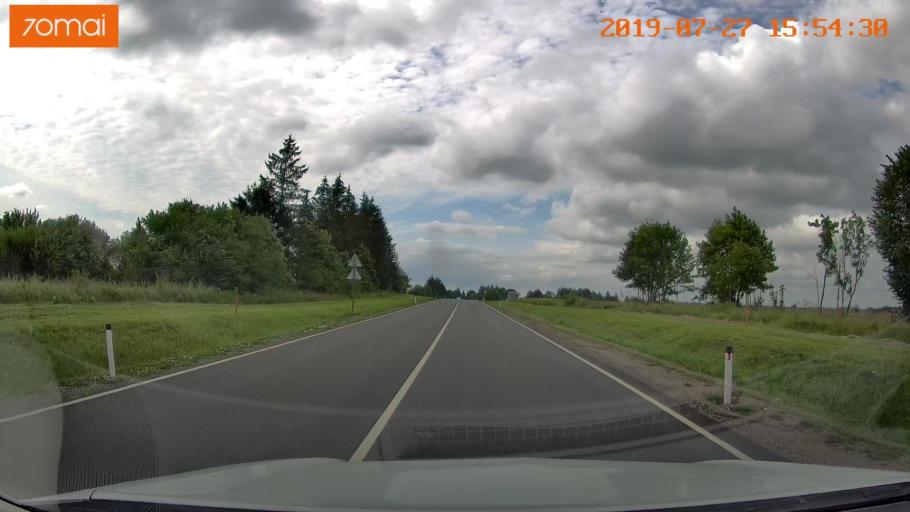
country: RU
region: Kaliningrad
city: Chernyakhovsk
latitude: 54.6080
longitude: 21.9381
